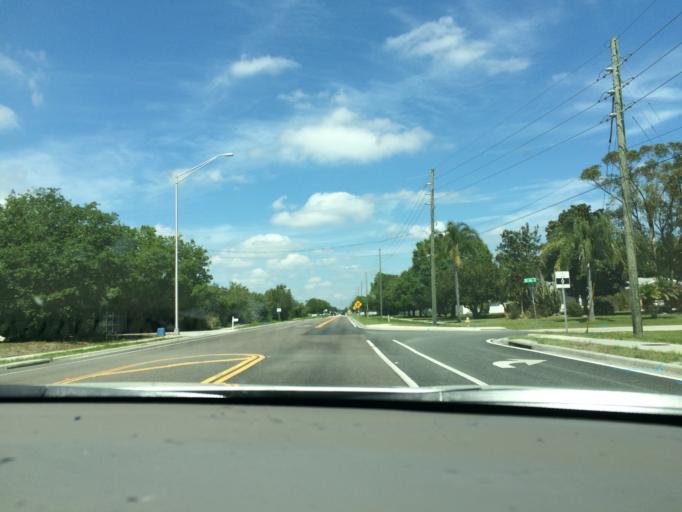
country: US
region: Florida
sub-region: Manatee County
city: Ellenton
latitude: 27.4890
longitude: -82.4337
